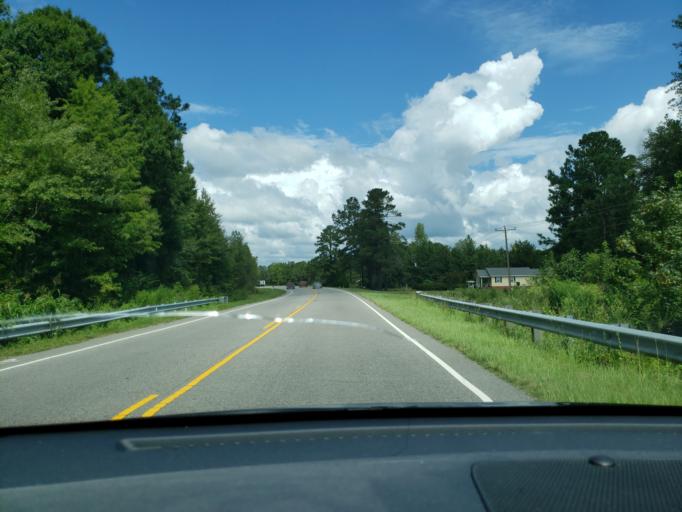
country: US
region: North Carolina
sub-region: Columbus County
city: Brunswick
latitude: 34.2358
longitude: -78.7532
